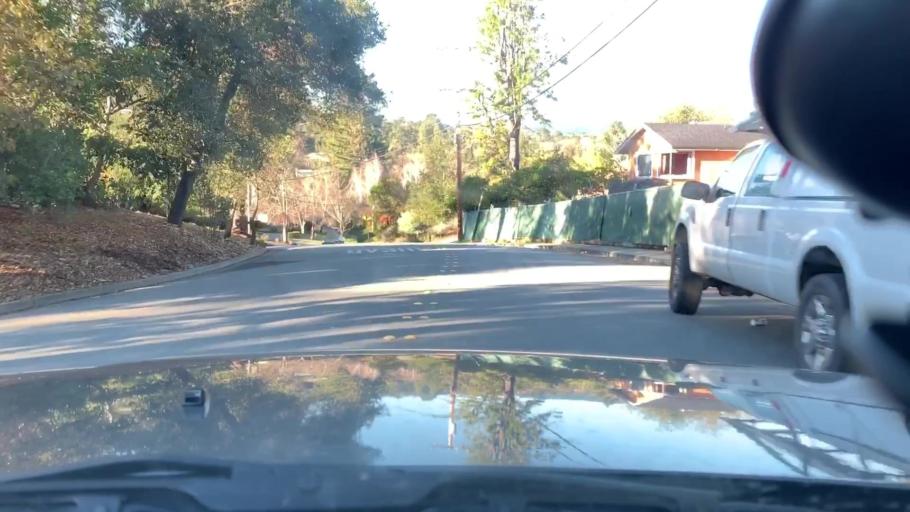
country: US
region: California
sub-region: San Mateo County
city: Ladera
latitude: 37.4010
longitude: -122.1967
